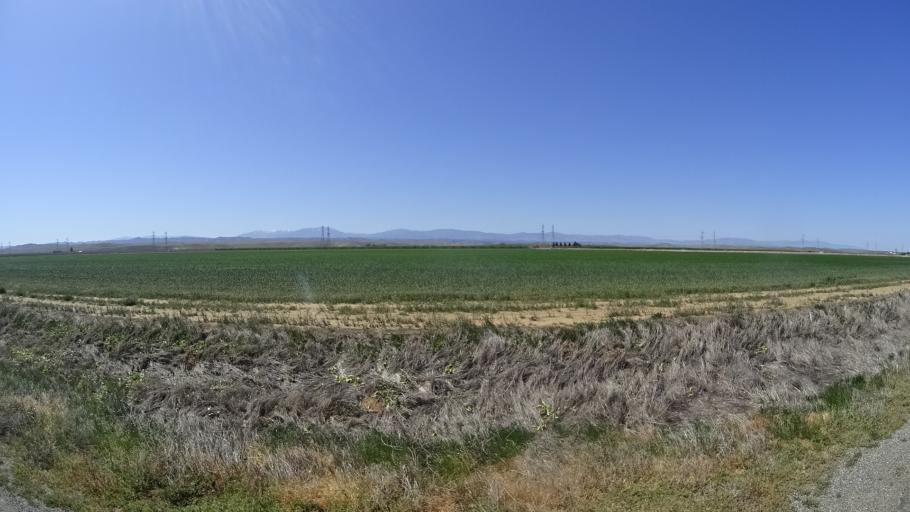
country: US
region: California
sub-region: Glenn County
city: Willows
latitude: 39.5154
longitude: -122.2774
